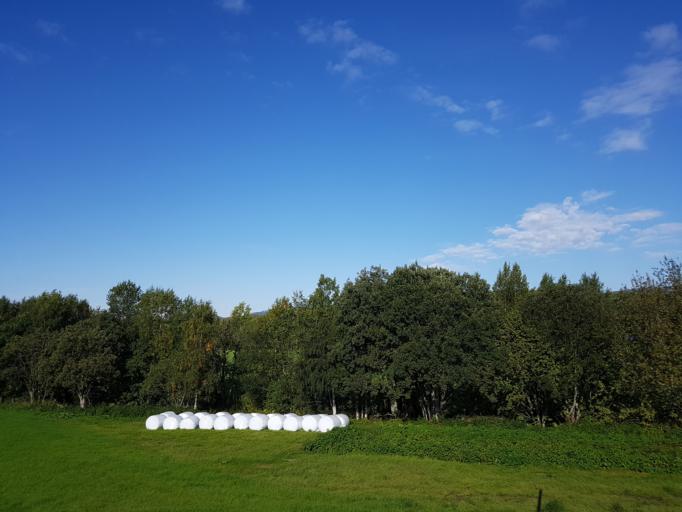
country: NO
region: Sor-Trondelag
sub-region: Trondheim
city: Trondheim
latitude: 63.6197
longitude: 10.2375
